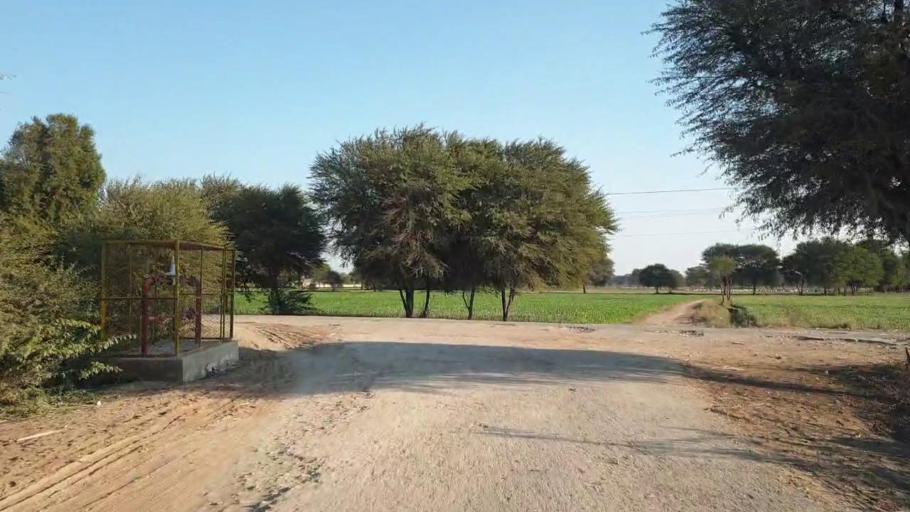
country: PK
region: Sindh
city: Shahpur Chakar
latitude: 26.1254
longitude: 68.5598
